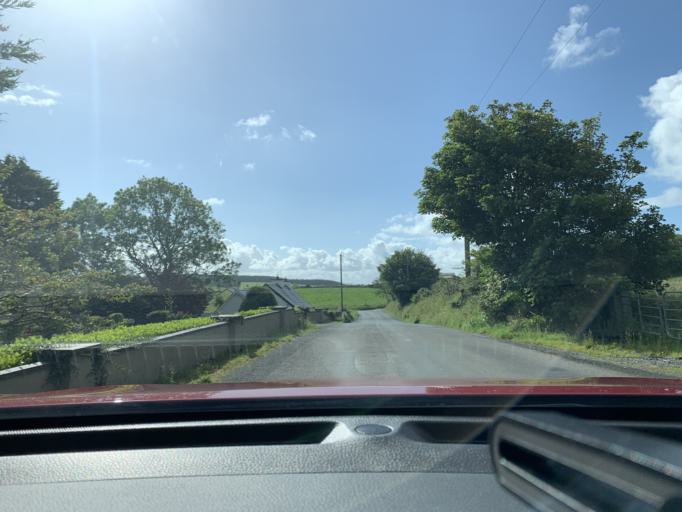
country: IE
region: Connaught
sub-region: Sligo
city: Strandhill
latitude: 54.3547
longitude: -8.6058
